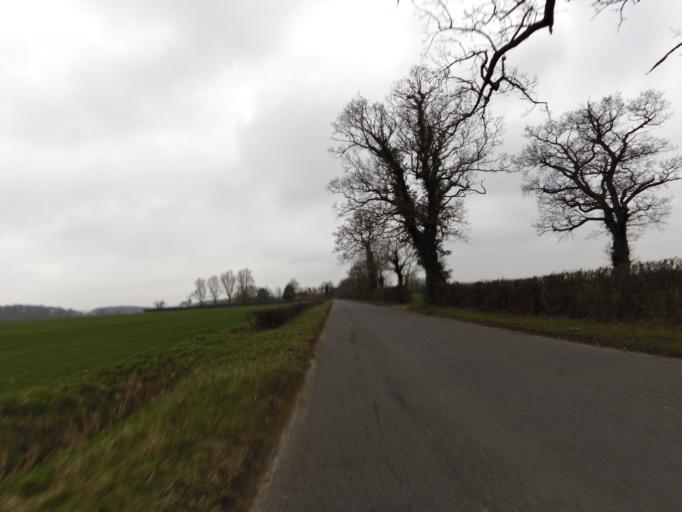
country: GB
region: England
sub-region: Suffolk
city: Framlingham
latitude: 52.1998
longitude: 1.3259
